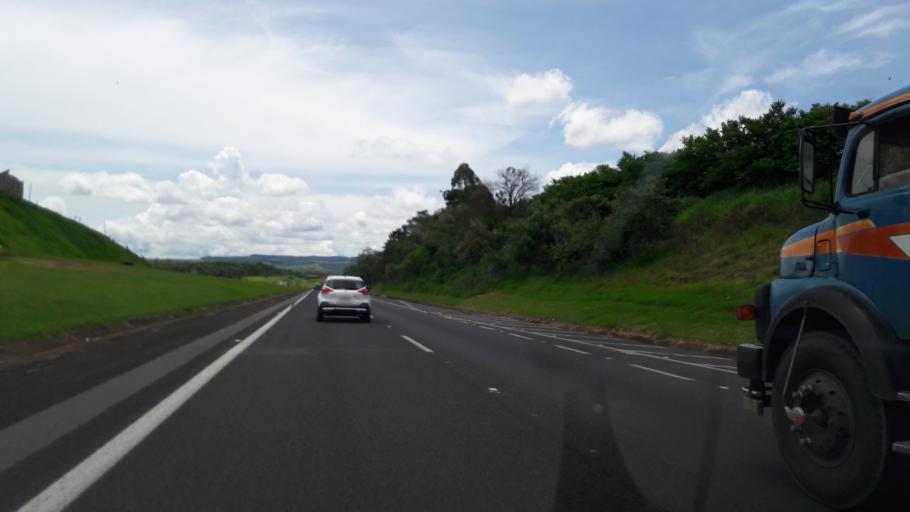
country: BR
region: Sao Paulo
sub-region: Itatinga
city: Itatinga
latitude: -23.1364
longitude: -48.4510
